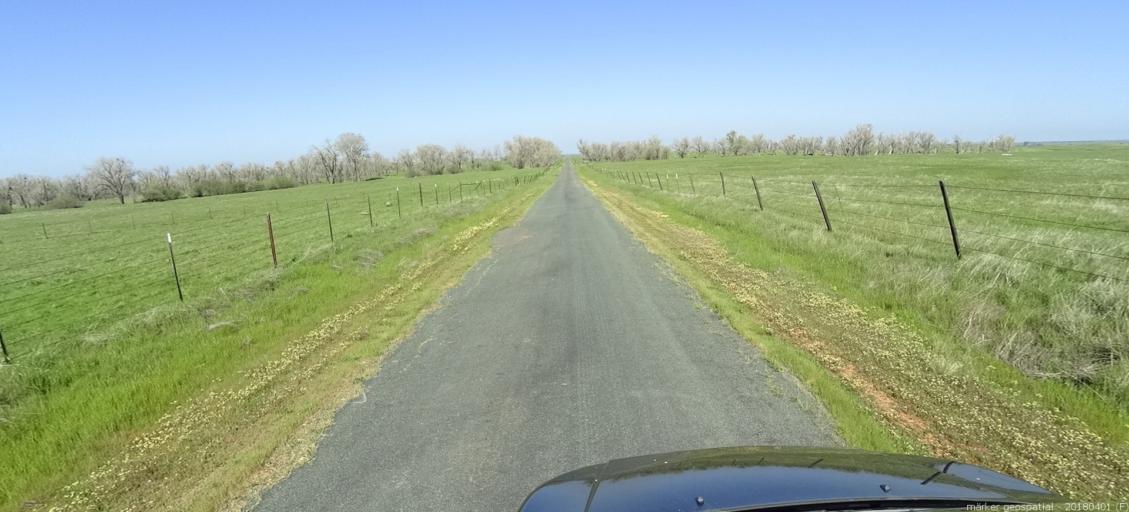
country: US
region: California
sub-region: Sacramento County
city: Rancho Murieta
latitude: 38.4573
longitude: -121.1045
